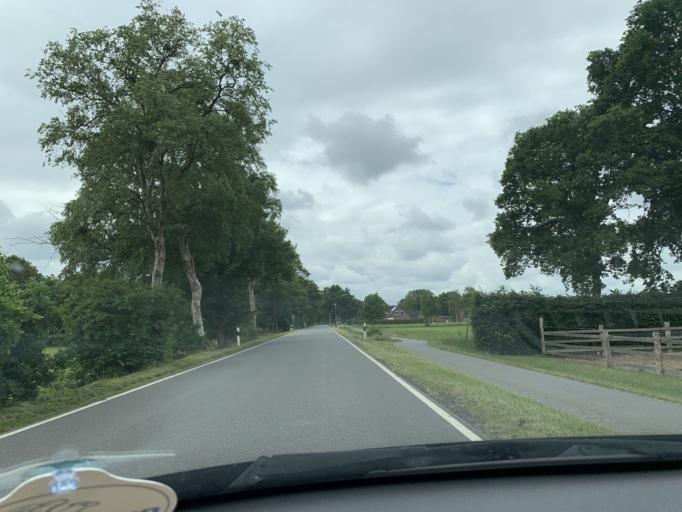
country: DE
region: Lower Saxony
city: Bockhorn
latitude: 53.3164
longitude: 8.0136
